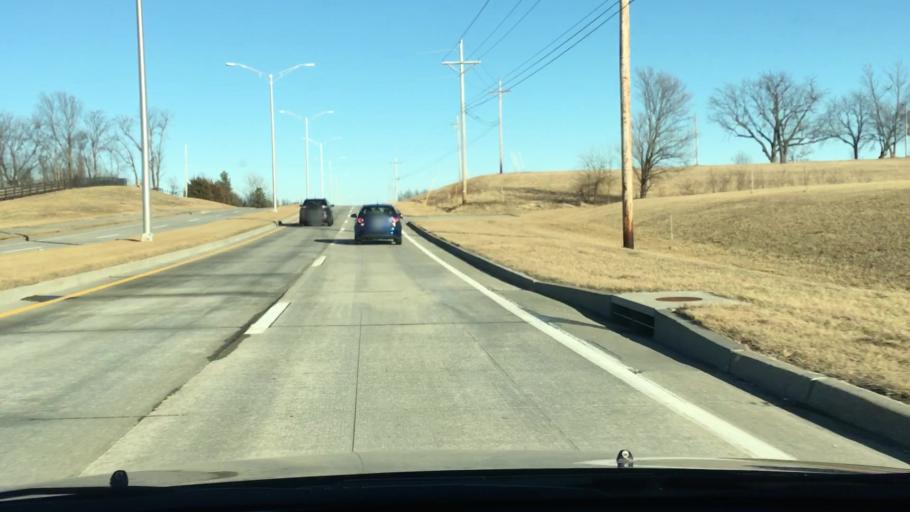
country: US
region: Missouri
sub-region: Cass County
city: Raymore
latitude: 38.8539
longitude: -94.4248
